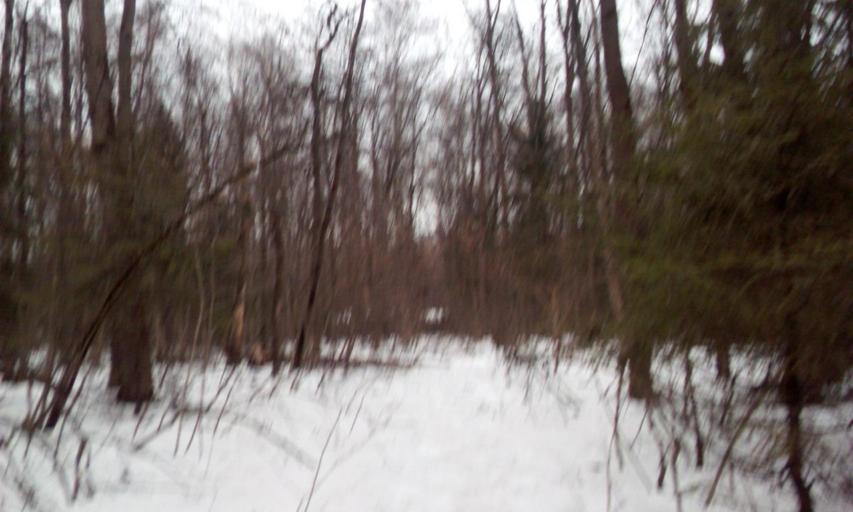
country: RU
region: Moskovskaya
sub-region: Leninskiy Rayon
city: Vnukovo
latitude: 55.6304
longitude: 37.2841
